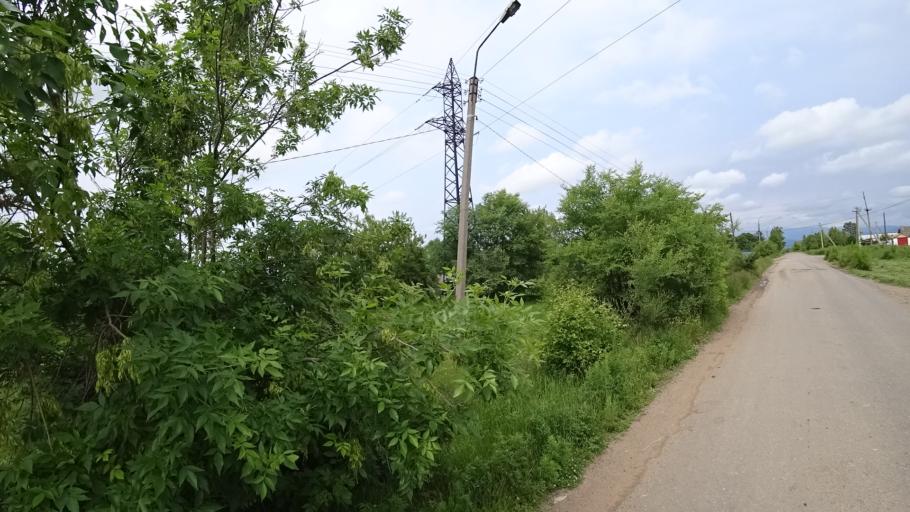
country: RU
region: Primorskiy
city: Novosysoyevka
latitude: 44.2317
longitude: 133.3603
